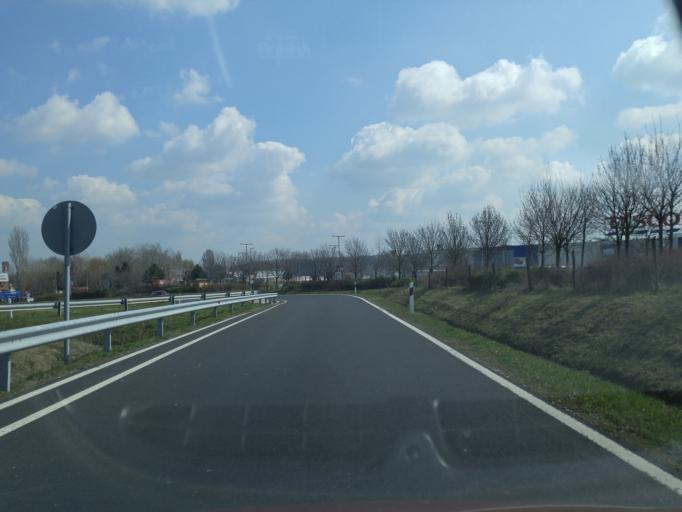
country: HU
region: Somogy
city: Siofok
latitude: 46.8941
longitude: 18.0549
